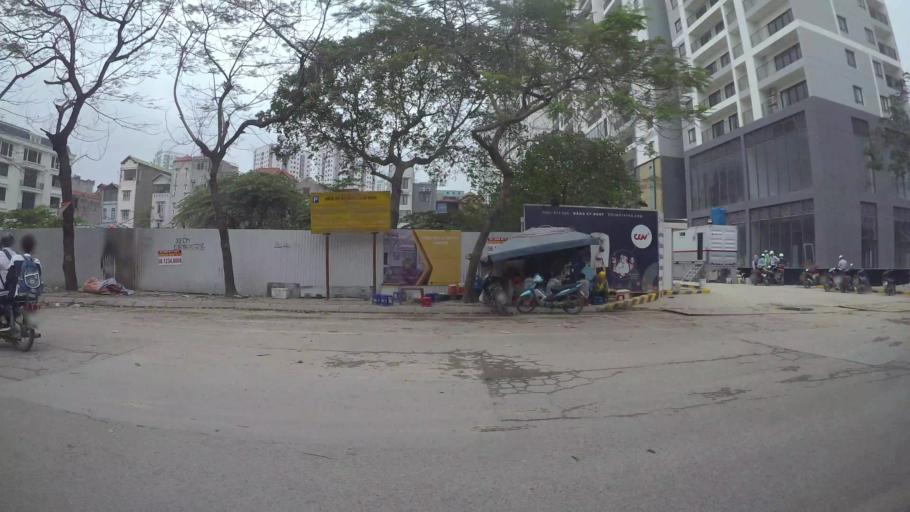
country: VN
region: Ha Noi
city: Tay Ho
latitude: 21.0684
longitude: 105.8030
